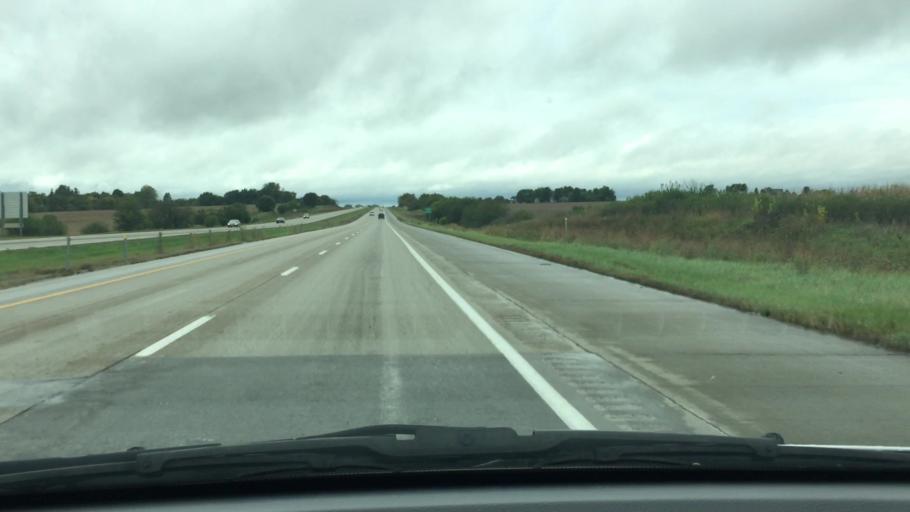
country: US
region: Iowa
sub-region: Polk County
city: Bondurant
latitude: 41.6782
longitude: -93.4131
